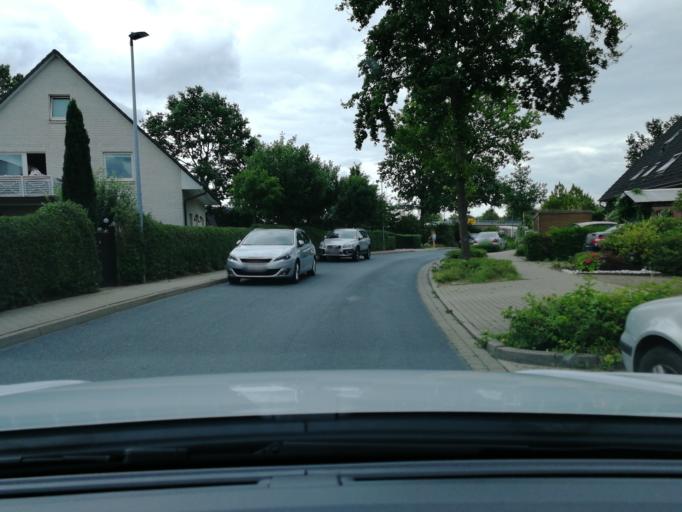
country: DE
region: Schleswig-Holstein
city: Schwarzenbek
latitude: 53.5131
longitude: 10.4877
